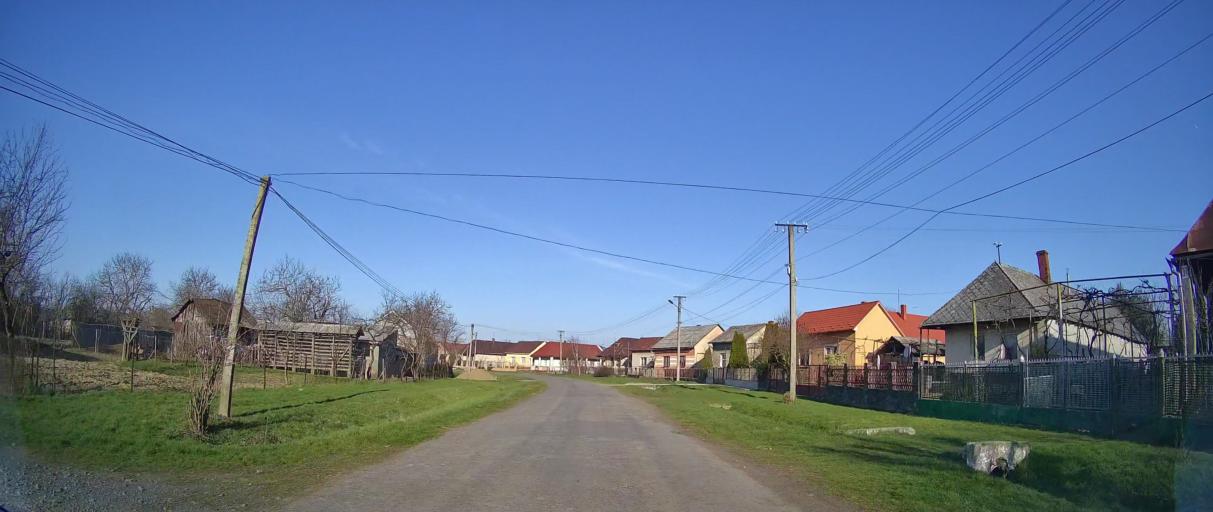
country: UA
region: Zakarpattia
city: Storozhnytsya
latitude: 48.5683
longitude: 22.1719
